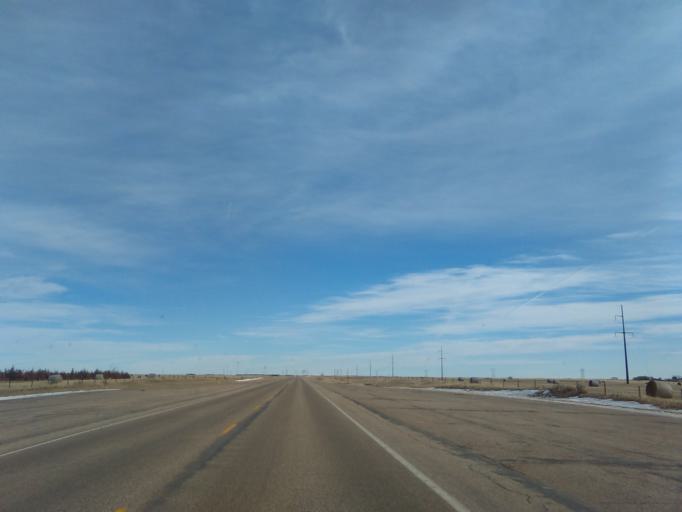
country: US
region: Wyoming
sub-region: Laramie County
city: Pine Bluffs
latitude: 41.4292
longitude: -104.3785
